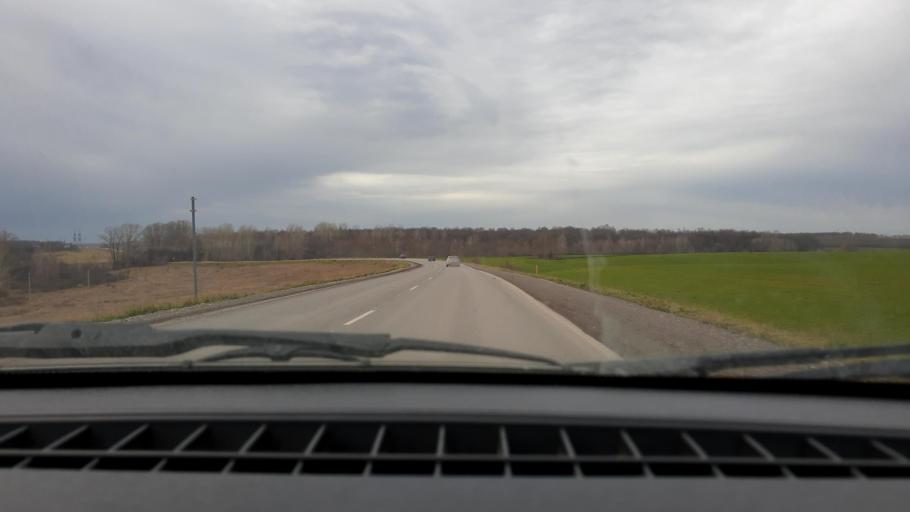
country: RU
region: Bashkortostan
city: Mikhaylovka
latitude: 54.8329
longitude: 55.9418
